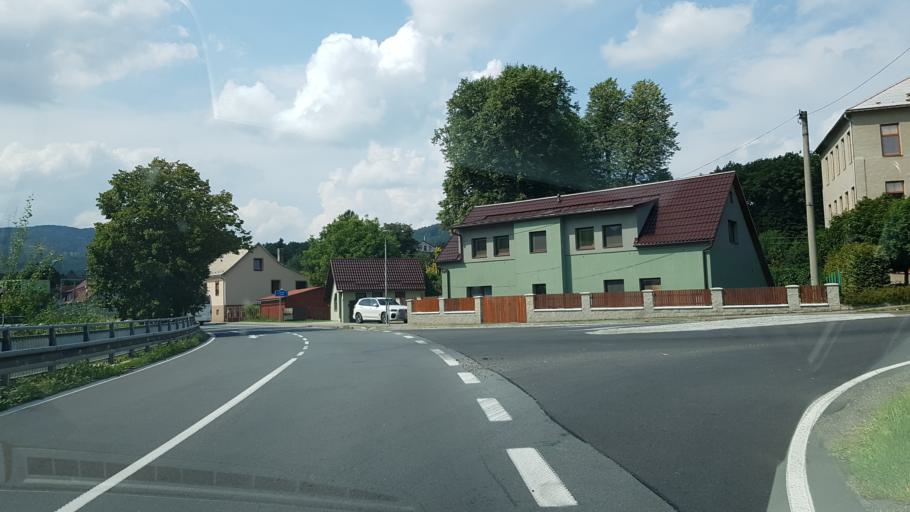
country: CZ
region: Olomoucky
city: Pisecna
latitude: 50.2727
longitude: 17.2532
